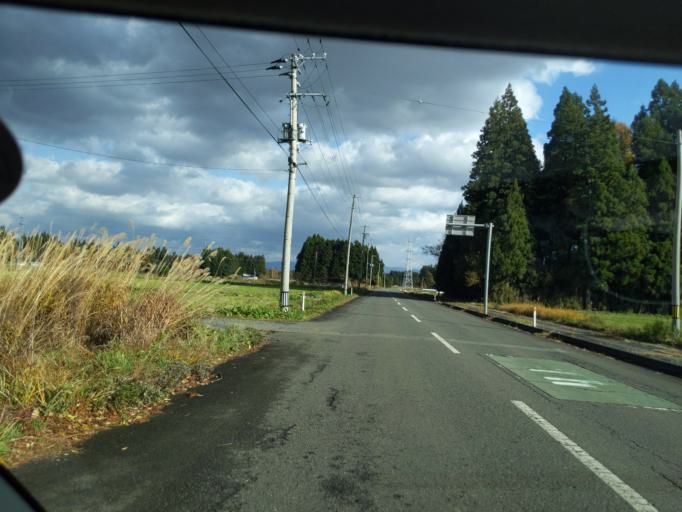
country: JP
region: Iwate
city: Mizusawa
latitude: 39.1162
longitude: 141.0006
